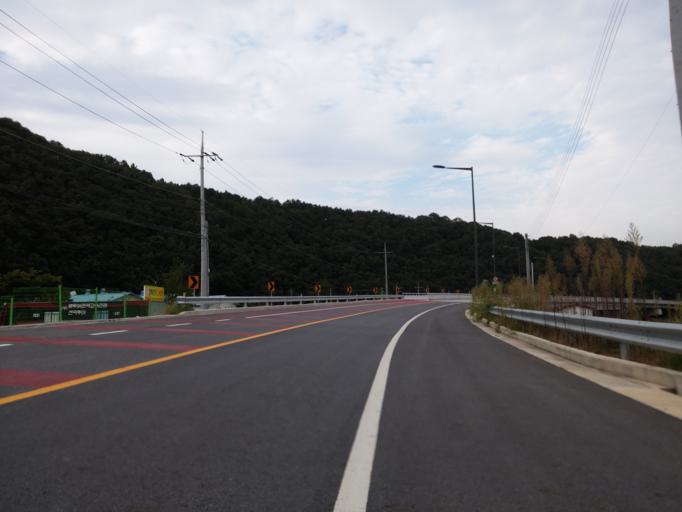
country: KR
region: Daejeon
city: Daejeon
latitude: 36.2277
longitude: 127.3024
